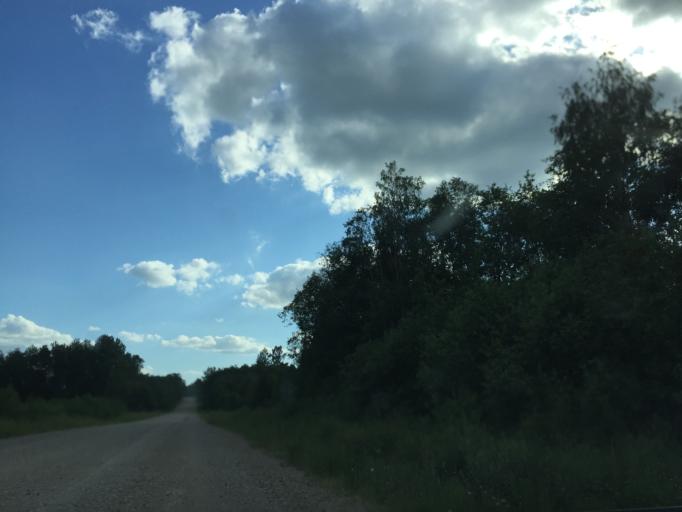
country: LV
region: Kandava
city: Kandava
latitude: 56.8713
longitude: 22.7676
